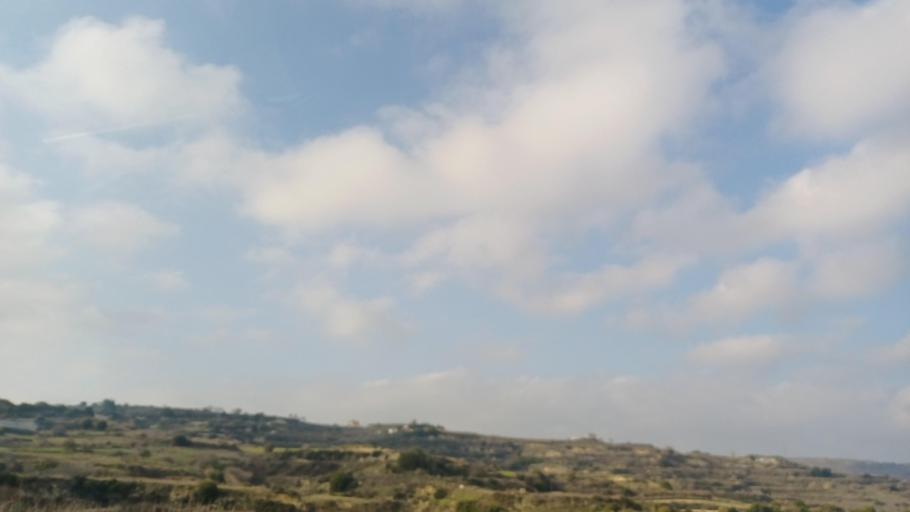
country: CY
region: Pafos
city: Mesogi
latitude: 34.8625
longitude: 32.4989
